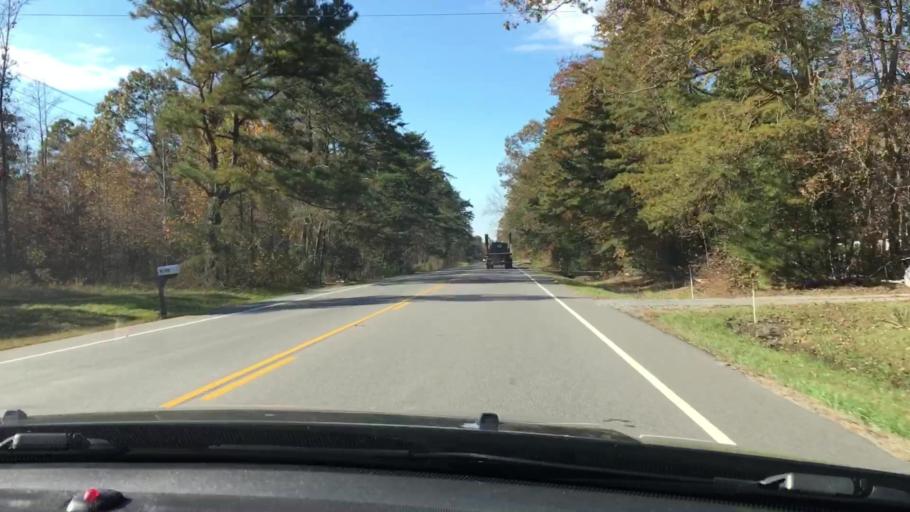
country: US
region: Virginia
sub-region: Hanover County
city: Hanover
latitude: 37.7959
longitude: -77.2483
